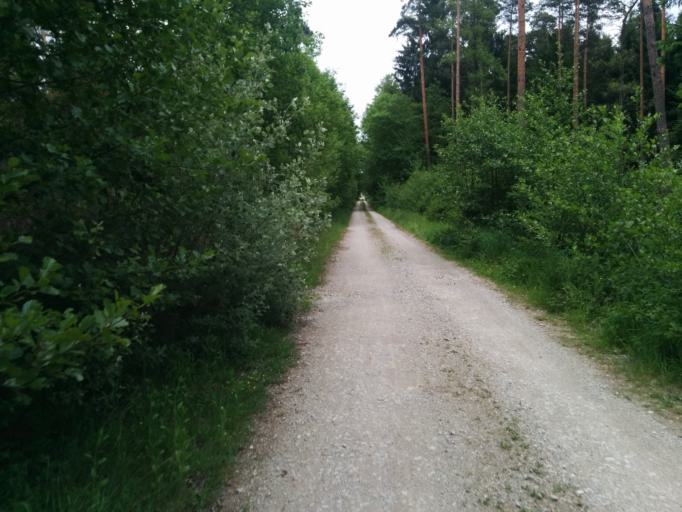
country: DE
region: Bavaria
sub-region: Regierungsbezirk Mittelfranken
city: Buckenhof
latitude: 49.5500
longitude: 11.0577
